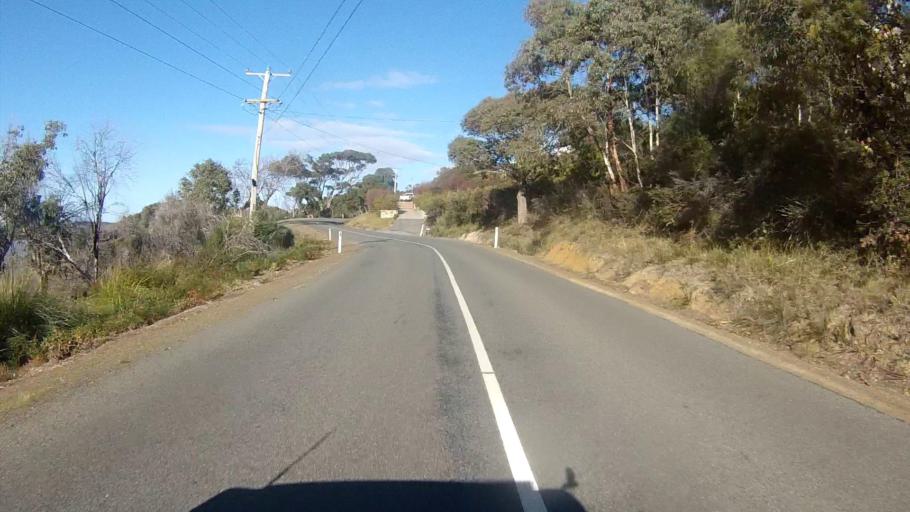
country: AU
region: Tasmania
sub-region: Clarence
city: Sandford
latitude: -43.0264
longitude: 147.9263
